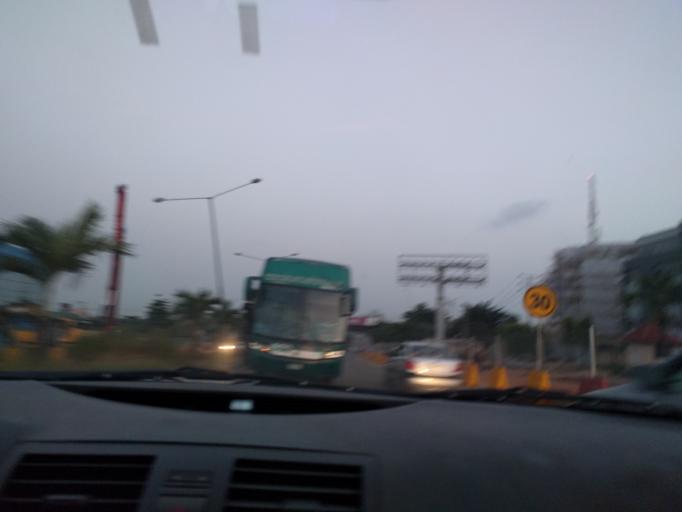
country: NG
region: Lagos
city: Oshodi
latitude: 6.5502
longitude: 3.3334
